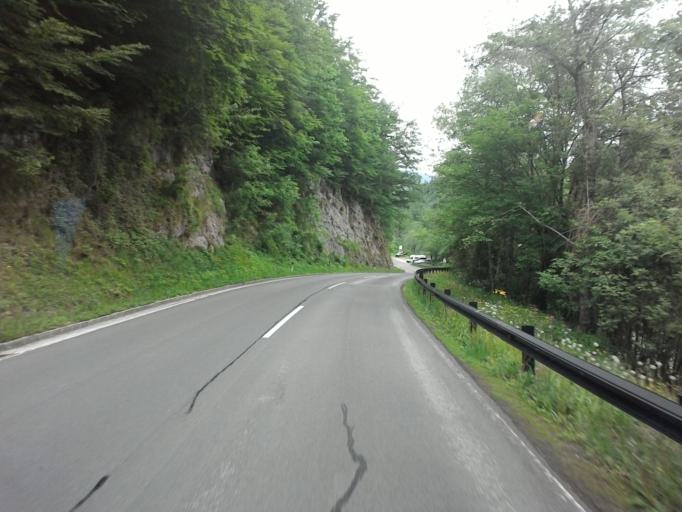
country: AT
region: Styria
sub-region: Politischer Bezirk Leoben
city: Hieflau
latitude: 47.6318
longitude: 14.7591
